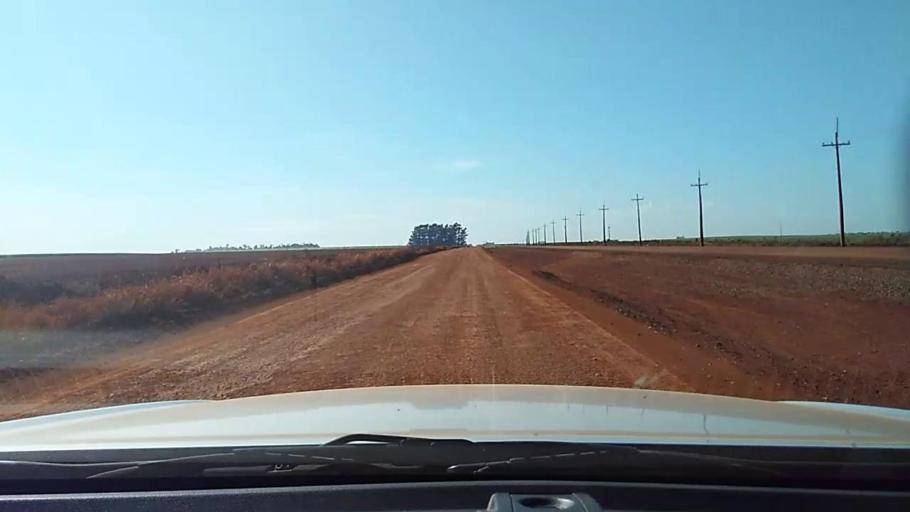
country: PY
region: Alto Parana
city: Naranjal
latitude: -25.9171
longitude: -55.4326
